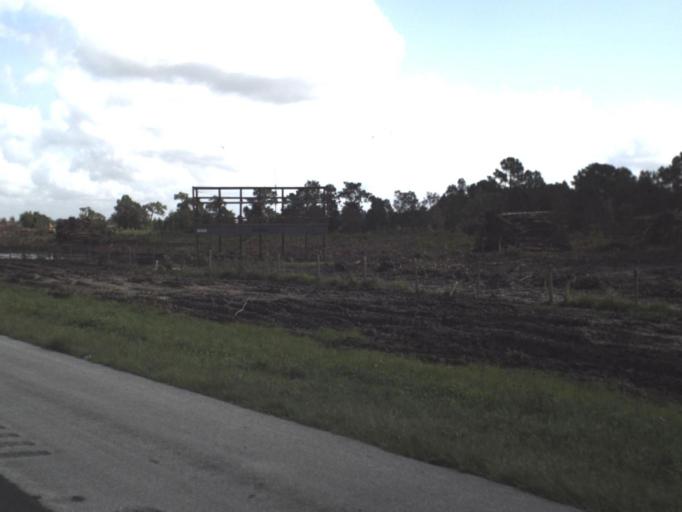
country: US
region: Florida
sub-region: Pasco County
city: Wesley Chapel
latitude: 28.2918
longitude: -82.3252
